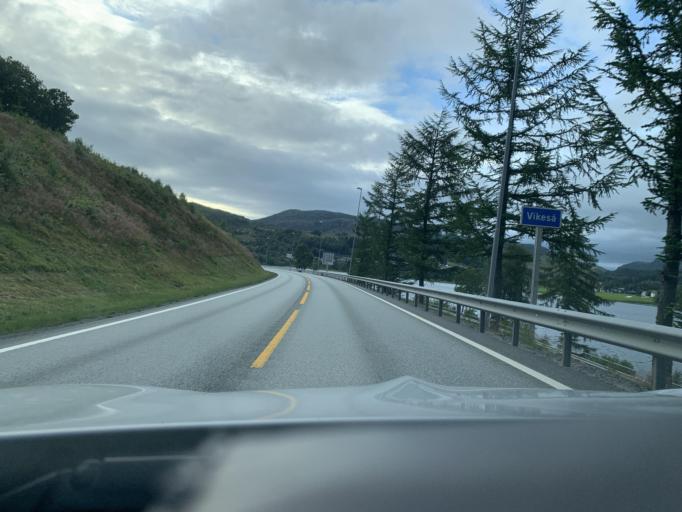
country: NO
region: Rogaland
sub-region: Bjerkreim
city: Vikesa
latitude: 58.6265
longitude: 6.0905
